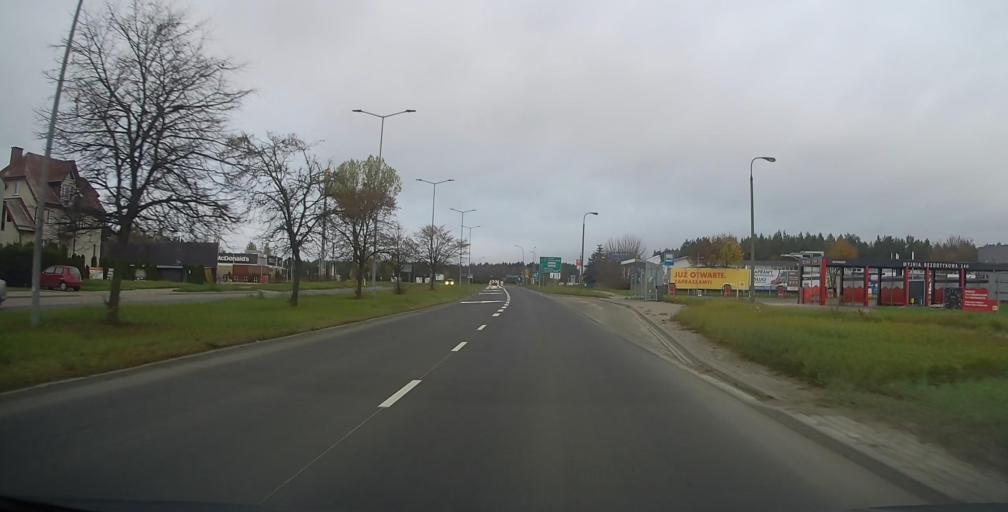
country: PL
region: Warmian-Masurian Voivodeship
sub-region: Powiat elcki
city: Elk
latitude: 53.8321
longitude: 22.3915
